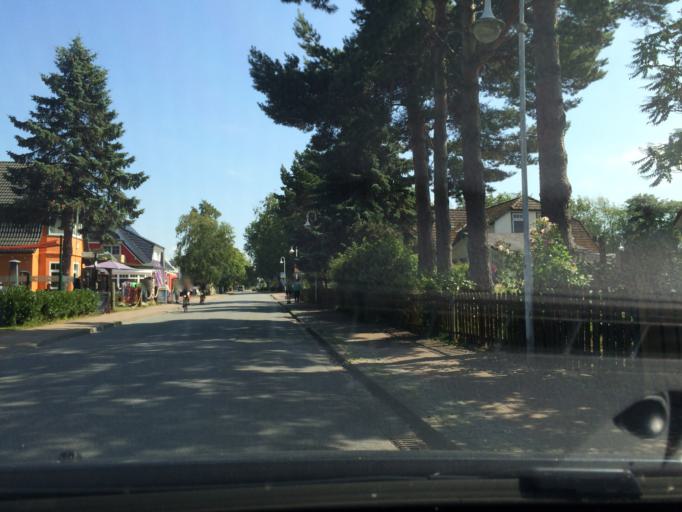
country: DE
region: Mecklenburg-Vorpommern
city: Ostseebad Prerow
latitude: 54.4459
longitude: 12.5752
